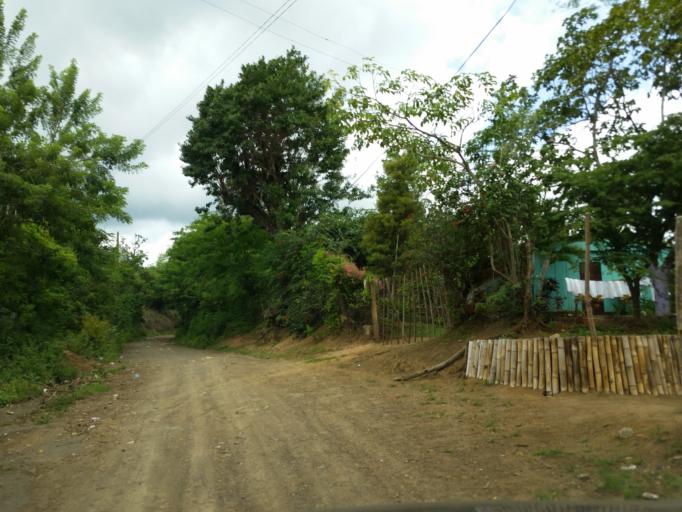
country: NI
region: Managua
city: Managua
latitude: 12.0862
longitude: -86.2737
